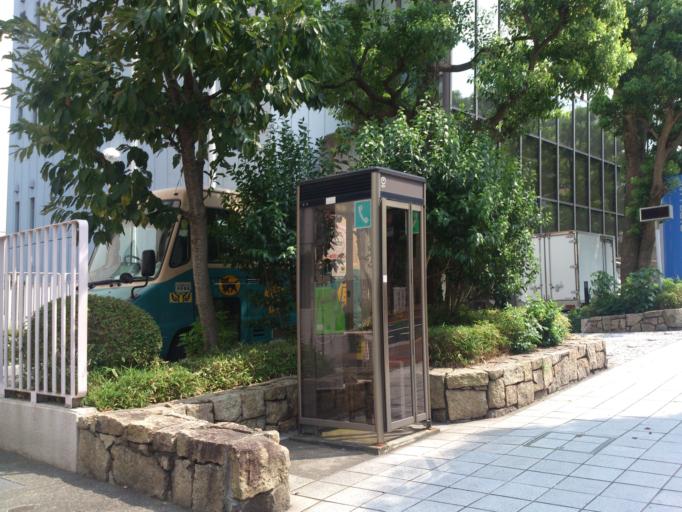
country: JP
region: Kanagawa
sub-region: Kawasaki-shi
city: Kawasaki
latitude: 35.5917
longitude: 139.7288
